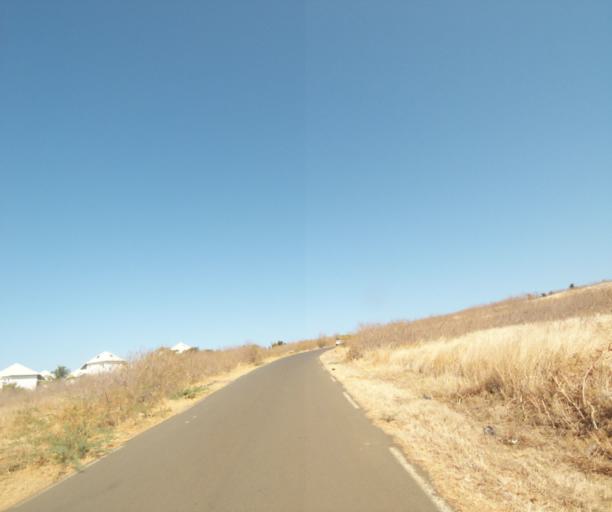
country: RE
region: Reunion
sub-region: Reunion
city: Trois-Bassins
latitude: -21.1046
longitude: 55.2534
